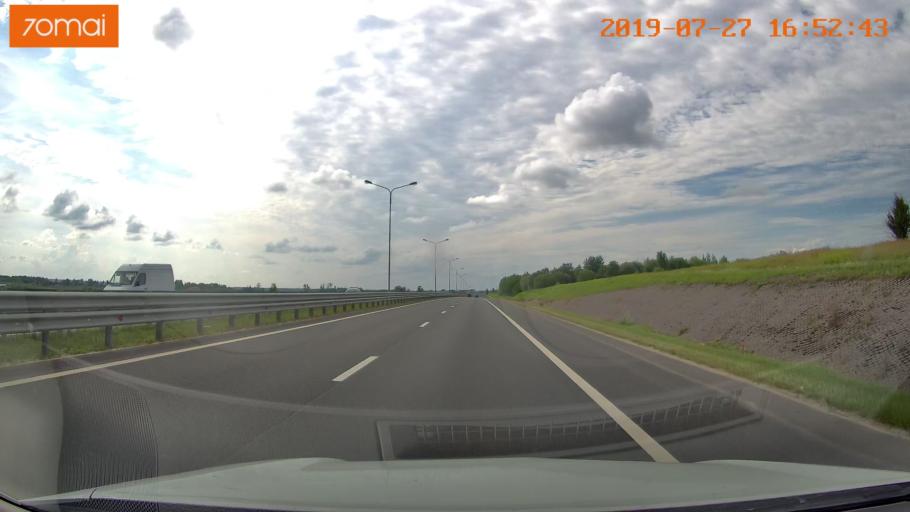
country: RU
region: Kaliningrad
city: Gvardeysk
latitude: 54.6840
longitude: 20.8500
